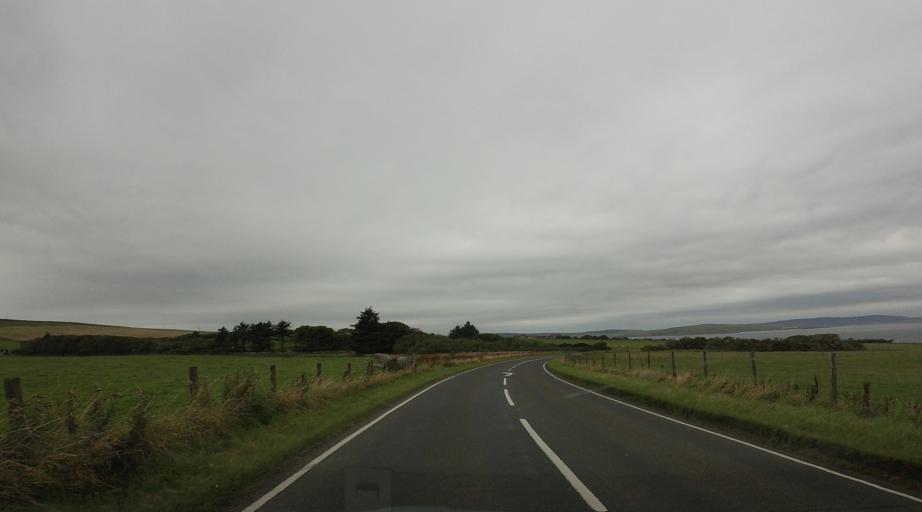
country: GB
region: Scotland
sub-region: Orkney Islands
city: Orkney
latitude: 58.9924
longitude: -2.9928
